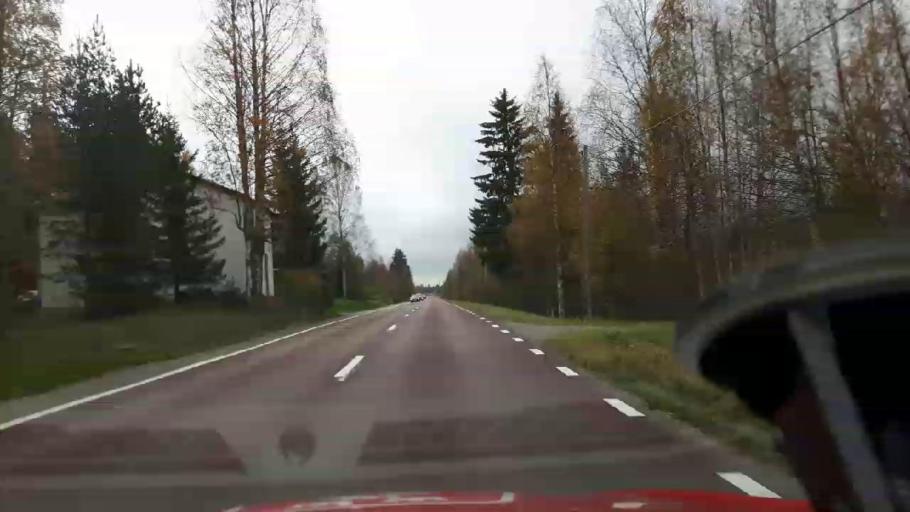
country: SE
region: Jaemtland
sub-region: Harjedalens Kommun
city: Sveg
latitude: 62.2908
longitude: 14.7926
